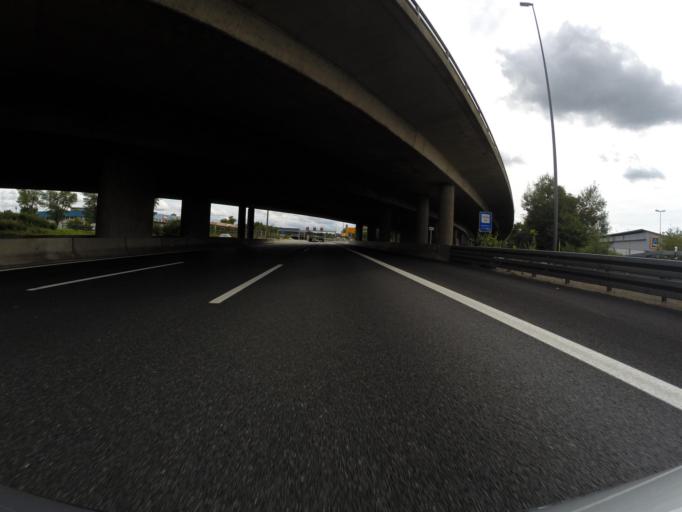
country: DE
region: Bavaria
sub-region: Upper Franconia
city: Bindlach
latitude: 49.9596
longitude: 11.6058
